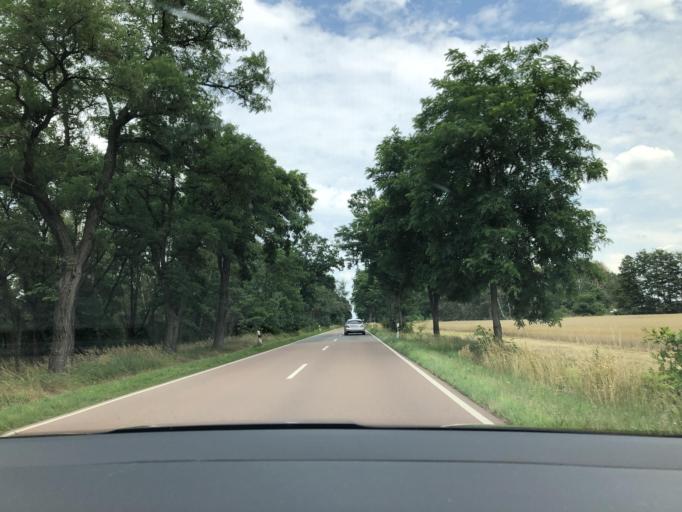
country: DE
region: Saxony-Anhalt
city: Lindau
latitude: 51.9908
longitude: 12.1313
